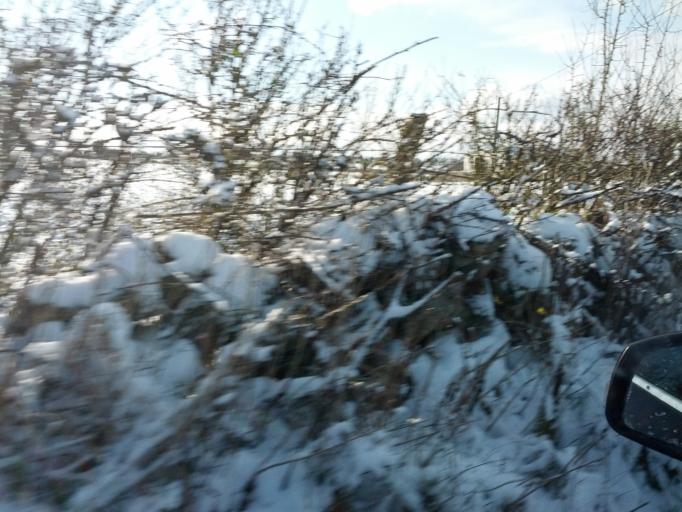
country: IE
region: Connaught
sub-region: County Galway
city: Athenry
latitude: 53.2015
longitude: -8.8085
